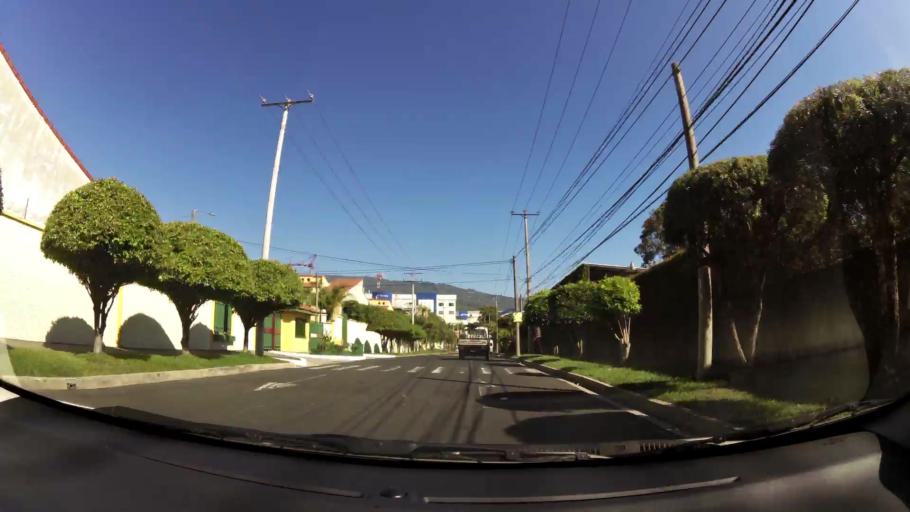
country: SV
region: La Libertad
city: Santa Tecla
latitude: 13.6758
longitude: -89.2761
